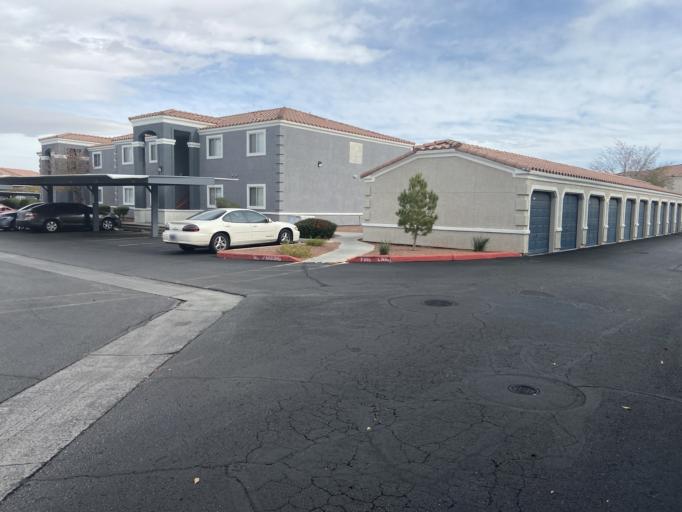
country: US
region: Nevada
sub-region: Clark County
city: North Las Vegas
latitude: 36.2197
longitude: -115.1585
